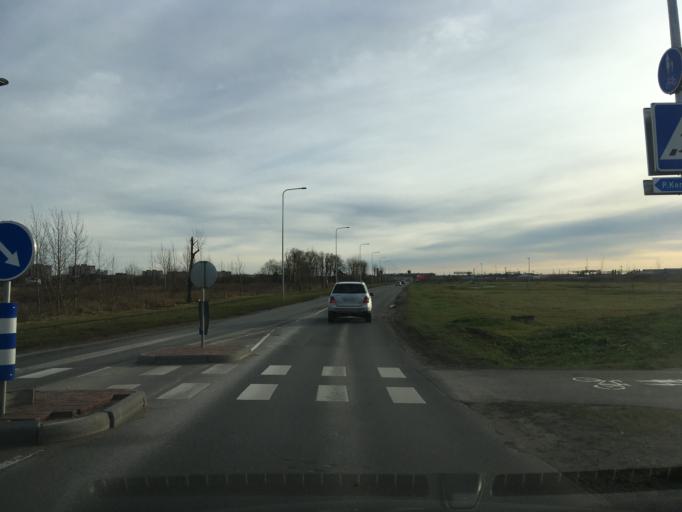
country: EE
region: Ida-Virumaa
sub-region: Narva linn
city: Narva
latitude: 59.3680
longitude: 28.1589
